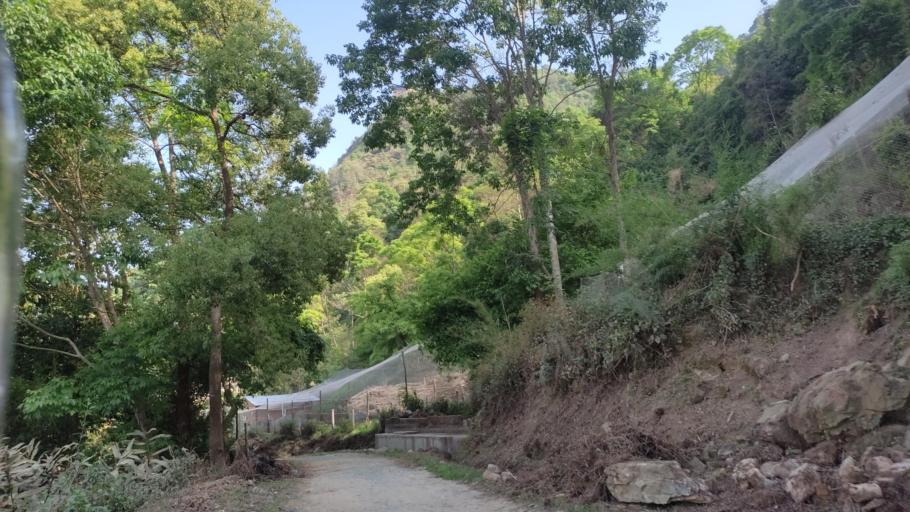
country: NP
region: Central Region
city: Kirtipur
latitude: 27.6573
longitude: 85.2648
